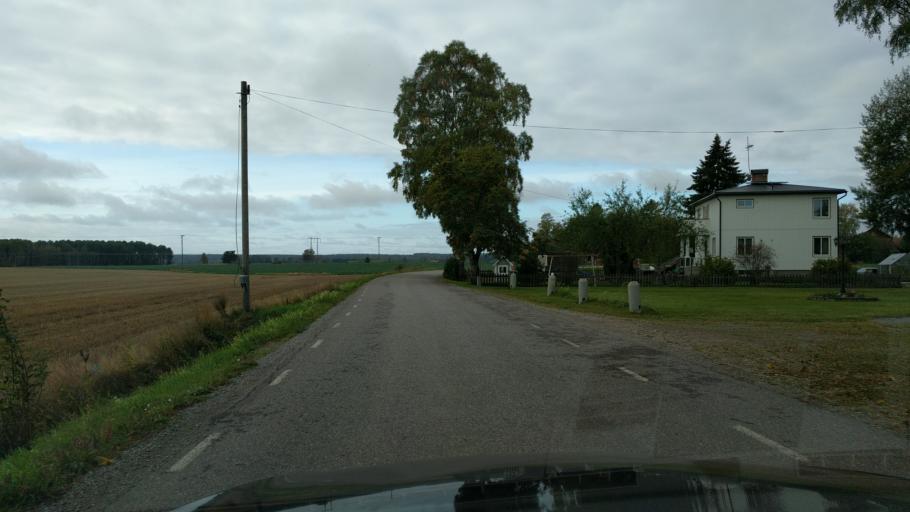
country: SE
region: Uppsala
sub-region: Osthammars Kommun
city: Bjorklinge
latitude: 60.1578
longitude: 17.5537
